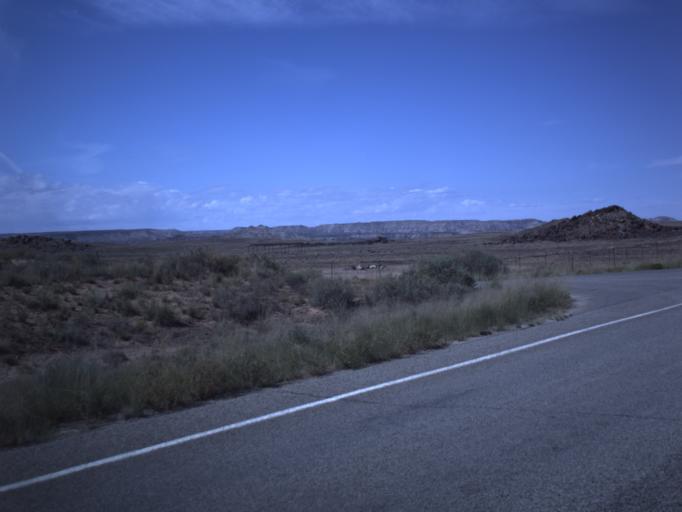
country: US
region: Colorado
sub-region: Montezuma County
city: Towaoc
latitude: 37.1680
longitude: -109.0828
